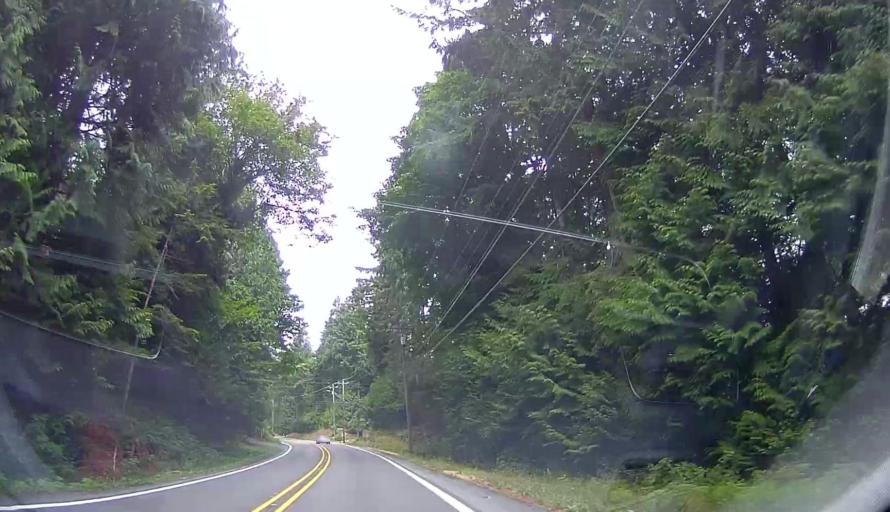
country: US
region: Washington
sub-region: Snohomish County
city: Tulalip
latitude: 48.1089
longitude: -122.3310
